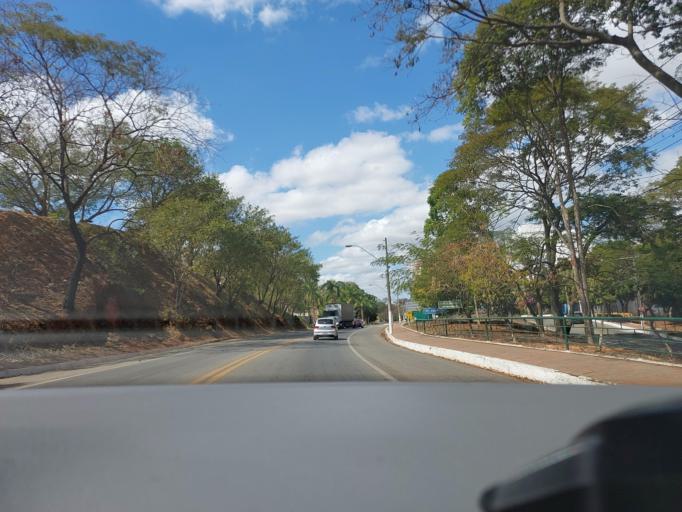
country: BR
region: Minas Gerais
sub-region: Muriae
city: Muriae
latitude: -21.1268
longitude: -42.3701
